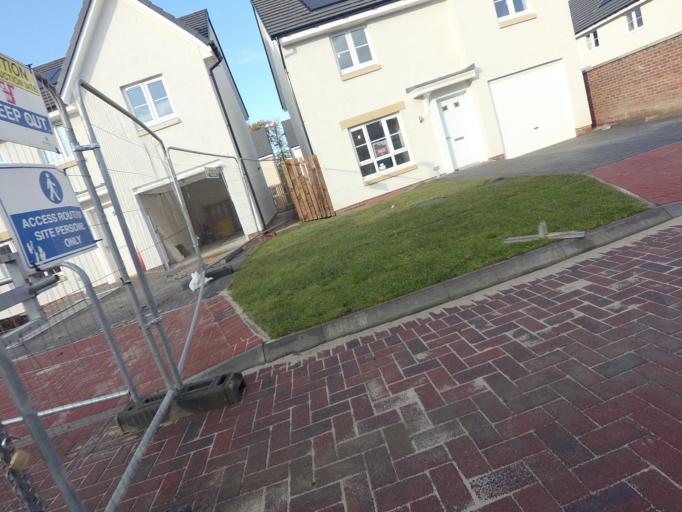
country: GB
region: Scotland
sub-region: West Lothian
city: West Calder
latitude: 55.8632
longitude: -3.5383
